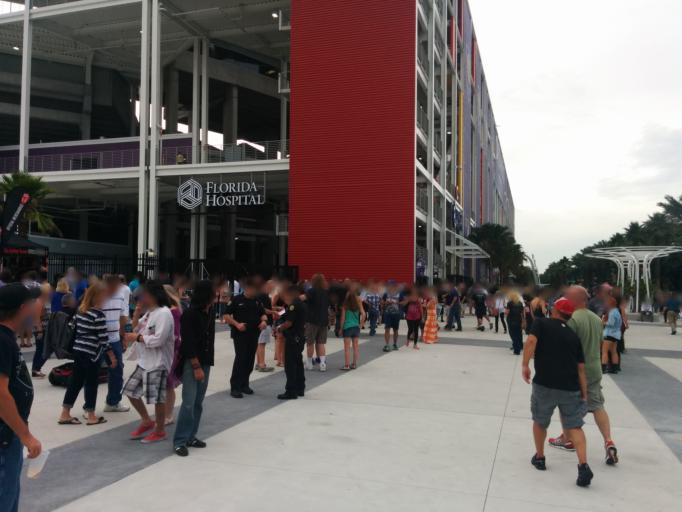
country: US
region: Florida
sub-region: Orange County
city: Orlando
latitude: 28.5380
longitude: -81.4016
